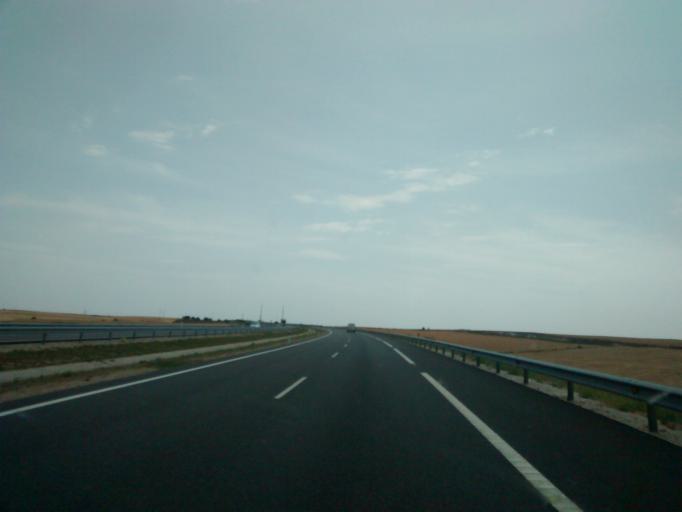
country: ES
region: Castille and Leon
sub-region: Provincia de Burgos
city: Isar
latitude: 42.3696
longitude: -3.8936
